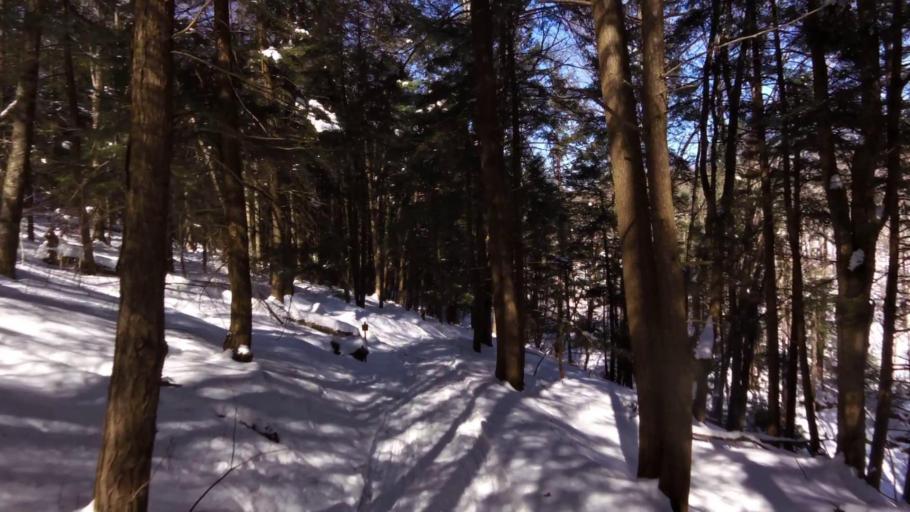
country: US
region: New York
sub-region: Allegany County
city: Cuba
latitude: 42.2819
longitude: -78.2327
